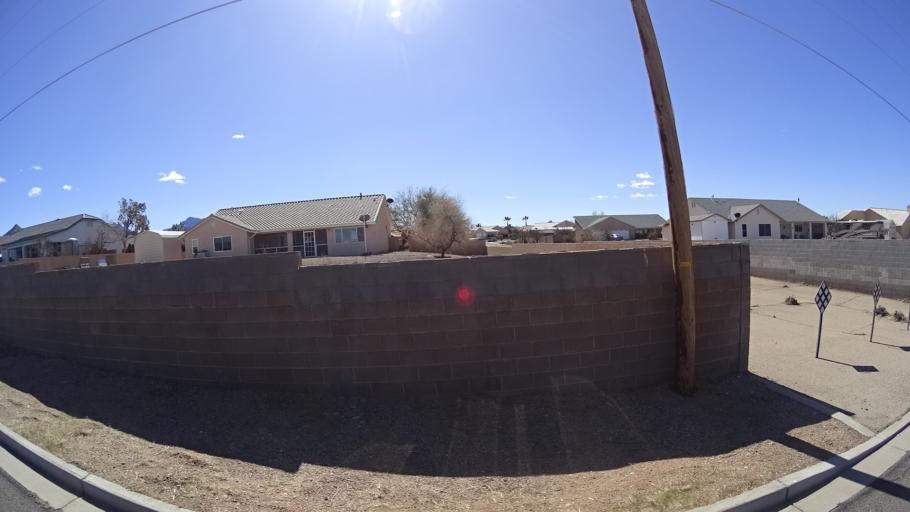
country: US
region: Arizona
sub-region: Mohave County
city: Kingman
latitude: 35.1958
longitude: -113.9817
